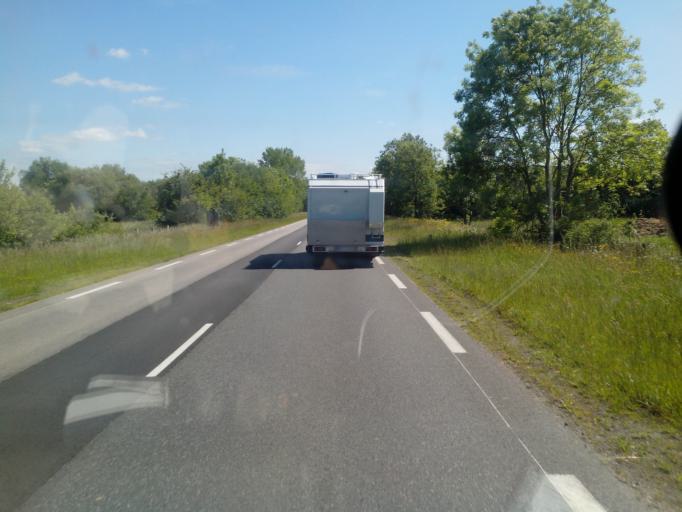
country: FR
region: Haute-Normandie
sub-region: Departement de l'Eure
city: Toutainville
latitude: 49.4094
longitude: 0.4246
